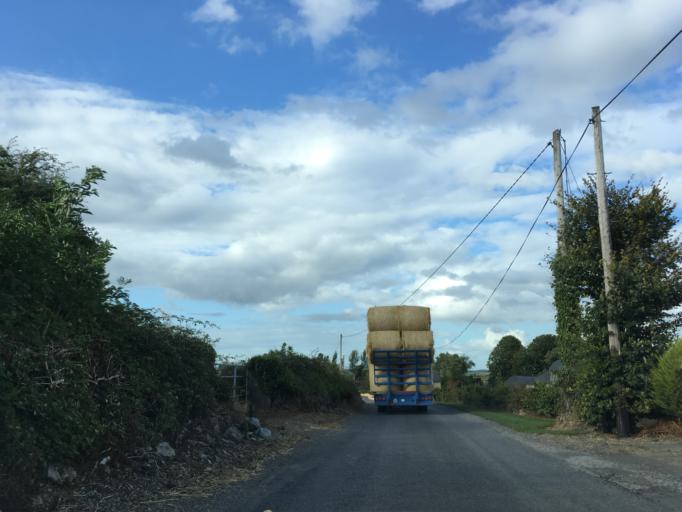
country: IE
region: Munster
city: Cahir
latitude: 52.3006
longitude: -7.9465
